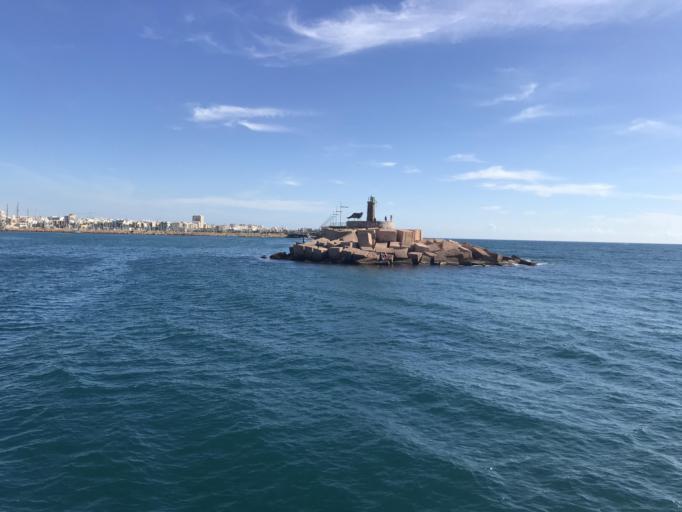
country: ES
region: Valencia
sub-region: Provincia de Alicante
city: Torrevieja
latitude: 37.9640
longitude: -0.6886
